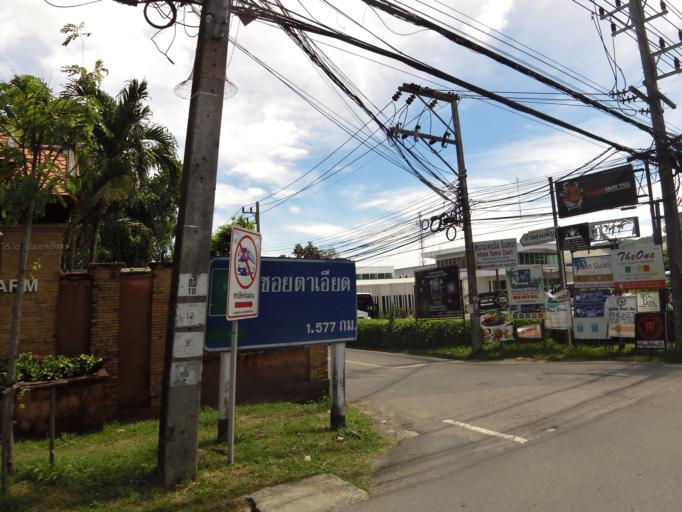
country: TH
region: Phuket
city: Ban Chalong
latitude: 7.8584
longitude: 98.3417
